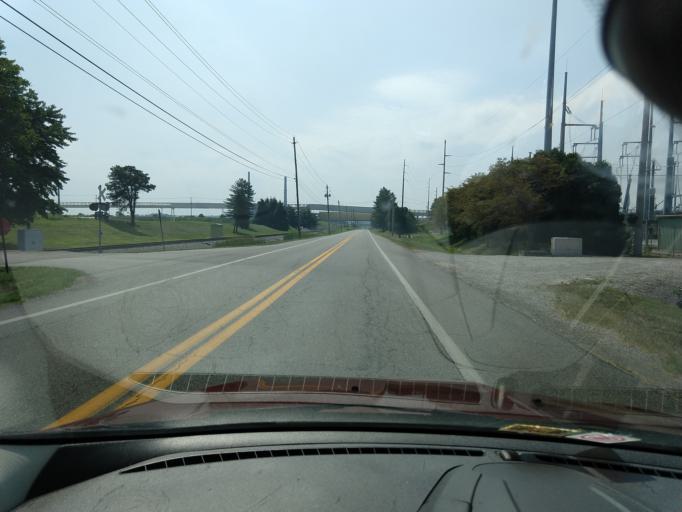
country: US
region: West Virginia
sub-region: Mason County
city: New Haven
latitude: 38.9767
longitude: -81.9405
